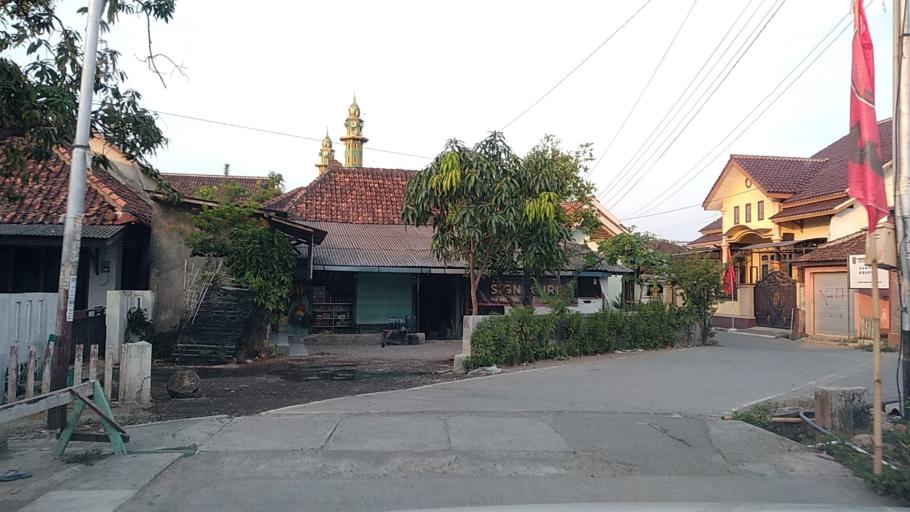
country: ID
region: Central Java
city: Semarang
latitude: -6.9559
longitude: 110.3143
